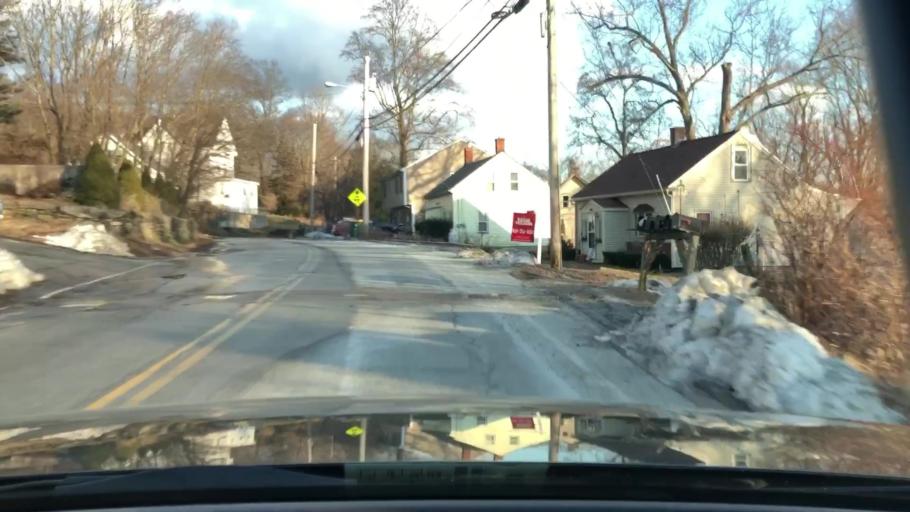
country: US
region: Massachusetts
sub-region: Worcester County
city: Millville
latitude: 42.0281
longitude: -71.5782
